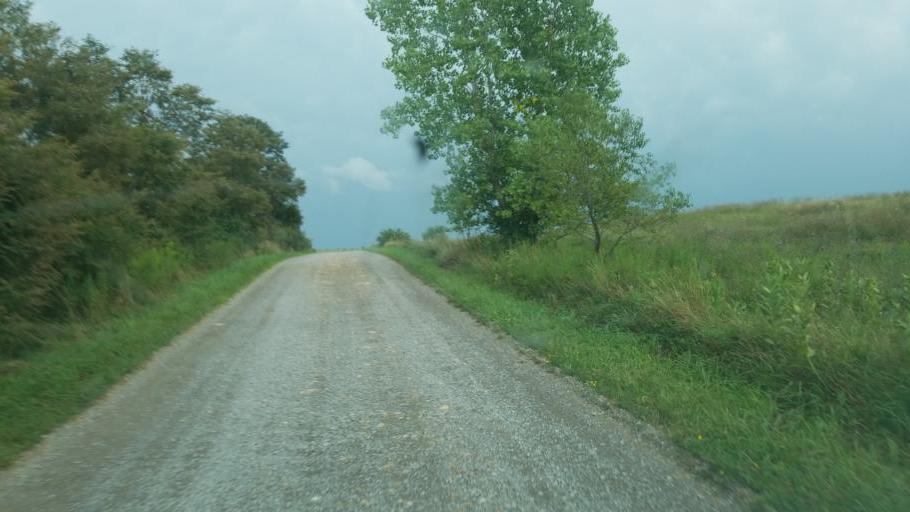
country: US
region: Pennsylvania
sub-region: Clarion County
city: Knox
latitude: 41.1455
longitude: -79.5078
